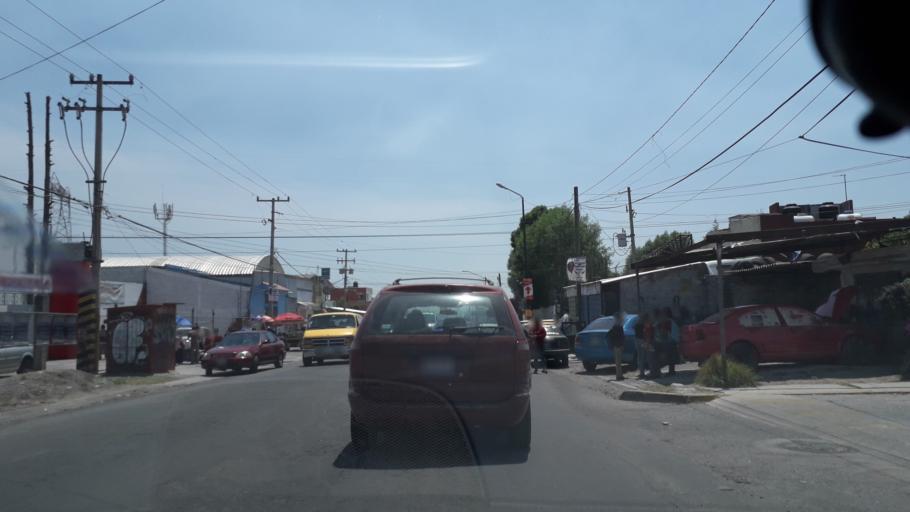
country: MX
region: Puebla
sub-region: Puebla
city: Primero de Mayo
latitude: 19.0763
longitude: -98.1126
